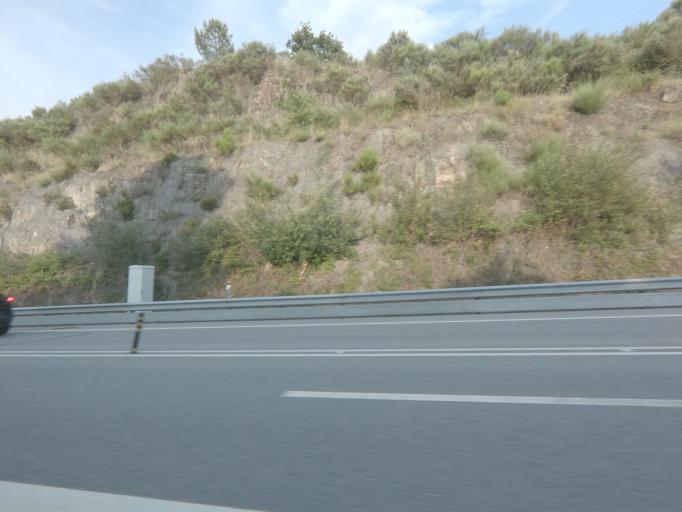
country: PT
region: Vila Real
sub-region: Vila Real
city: Vila Real
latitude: 41.2919
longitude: -7.7561
